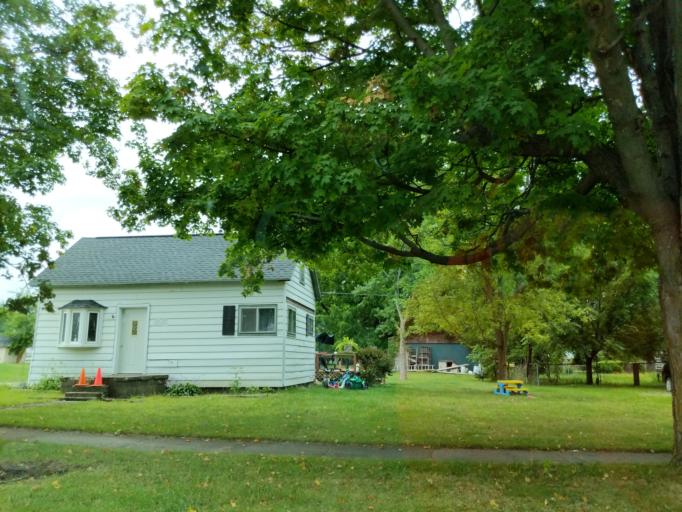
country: US
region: Michigan
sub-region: Lapeer County
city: Barnes Lake-Millers Lake
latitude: 43.3362
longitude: -83.3465
